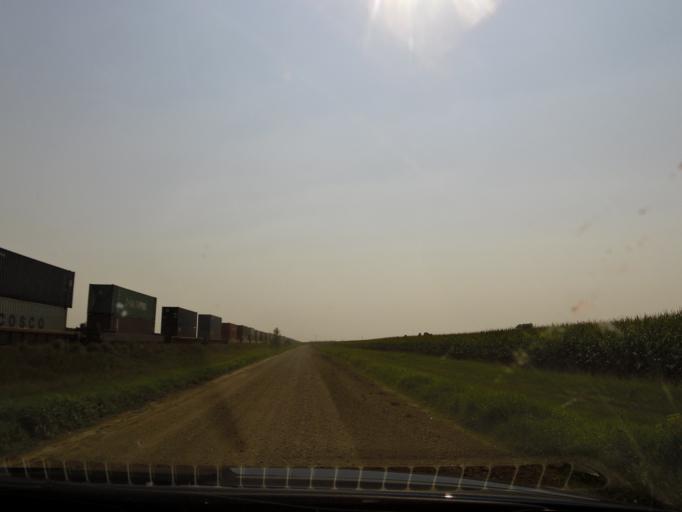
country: US
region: North Dakota
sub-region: Ransom County
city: Sheldon
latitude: 46.2591
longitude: -97.1185
